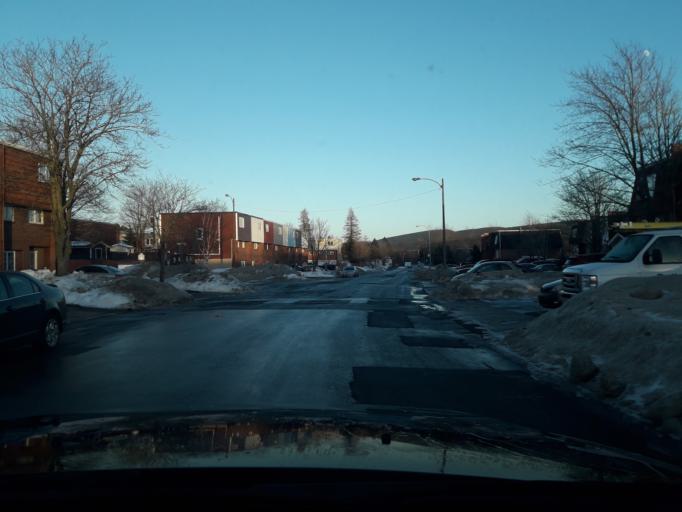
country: CA
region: Newfoundland and Labrador
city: Mount Pearl
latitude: 47.5243
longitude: -52.7655
